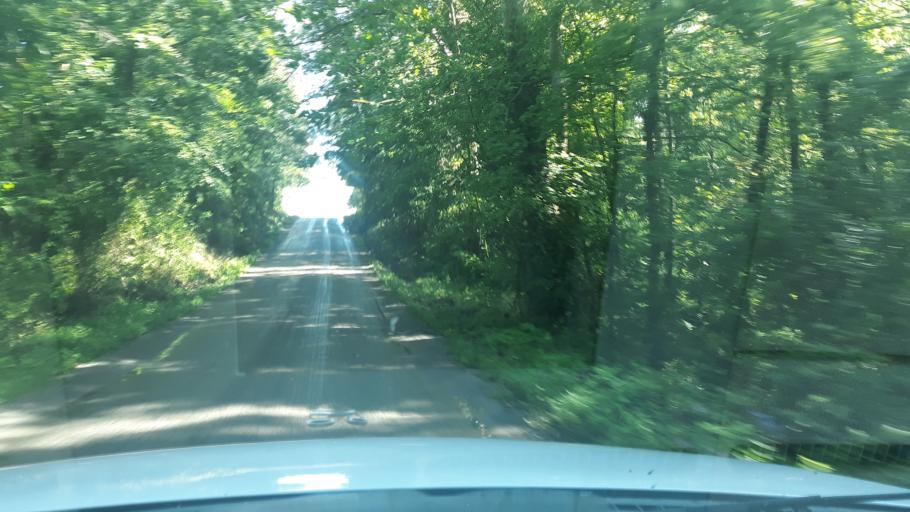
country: US
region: Illinois
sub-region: Saline County
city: Harrisburg
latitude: 37.8422
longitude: -88.5814
